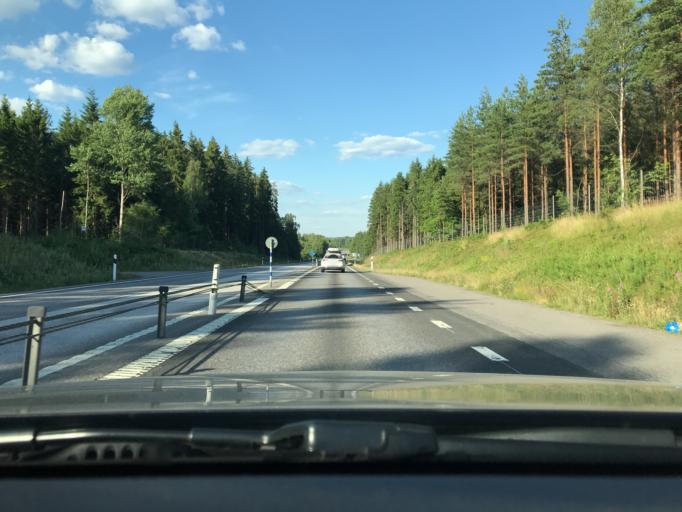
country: SE
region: Kronoberg
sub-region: Vaxjo Kommun
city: Rottne
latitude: 56.9643
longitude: 14.9582
